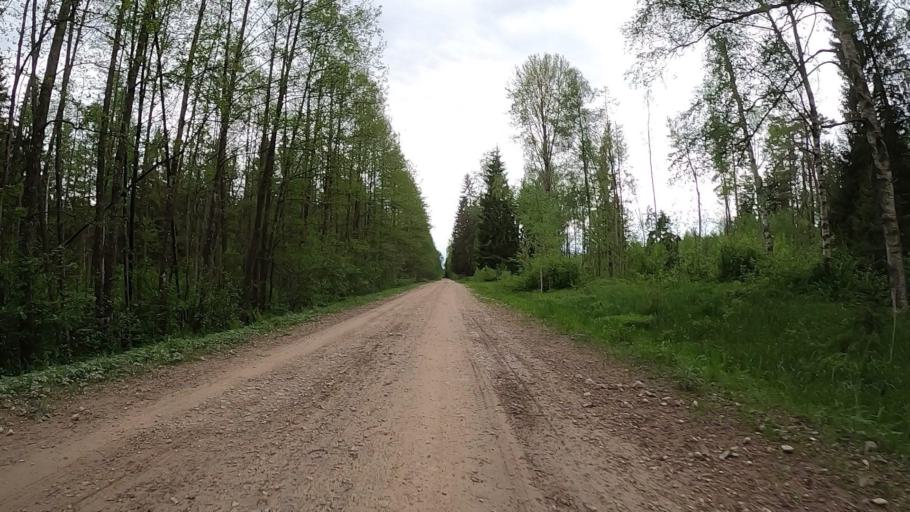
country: LV
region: Ozolnieku
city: Ozolnieki
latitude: 56.7778
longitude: 23.7681
